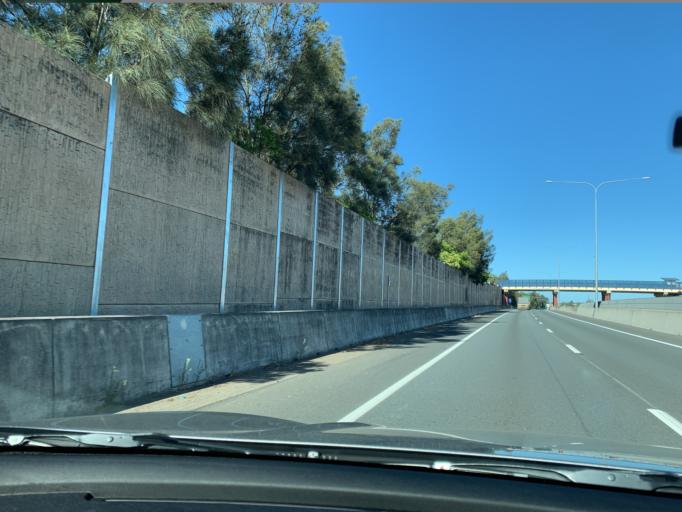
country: AU
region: Queensland
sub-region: Brisbane
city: Wynnum West
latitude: -27.4478
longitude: 153.1244
